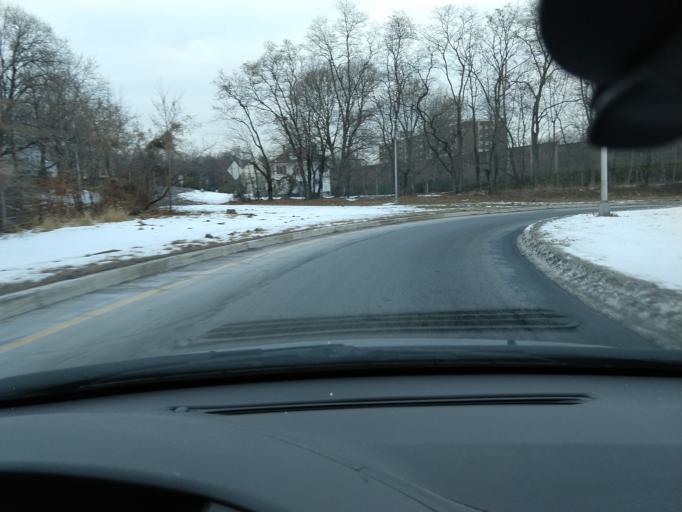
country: US
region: New Jersey
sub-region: Essex County
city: Orange
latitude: 40.7771
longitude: -74.2430
